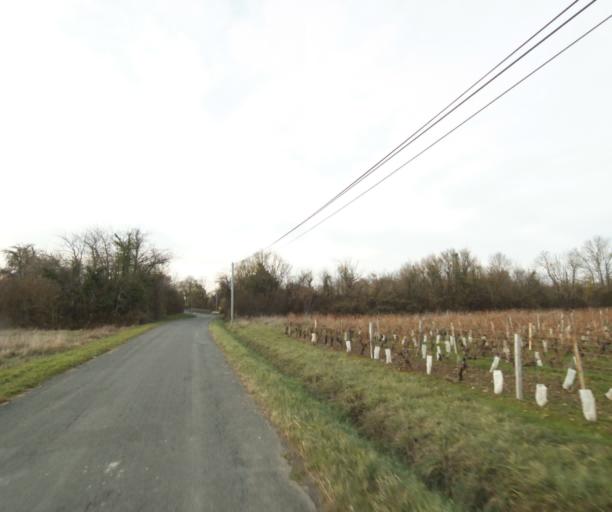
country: FR
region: Poitou-Charentes
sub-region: Departement de la Charente-Maritime
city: Fontcouverte
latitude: 45.7875
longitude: -0.5771
